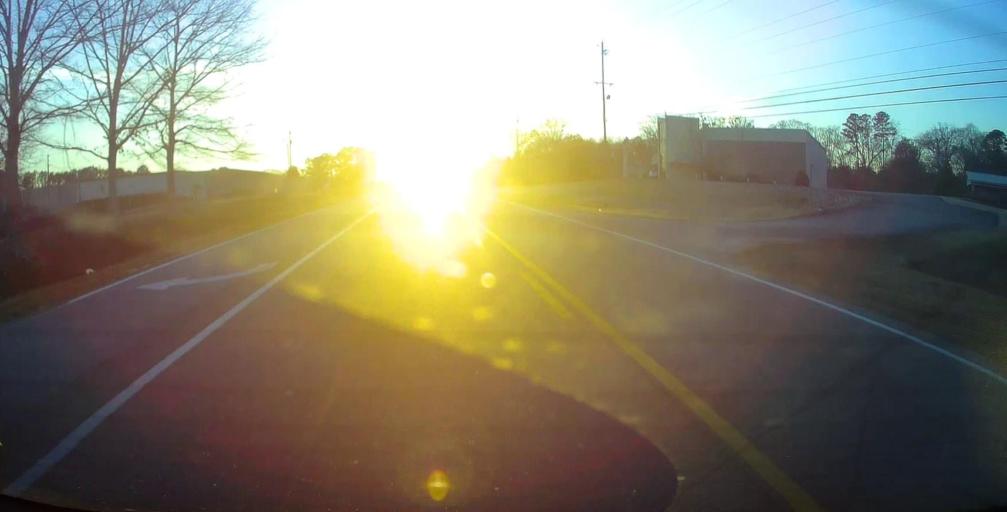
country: US
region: Georgia
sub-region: Troup County
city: La Grange
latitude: 33.0167
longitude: -85.0022
